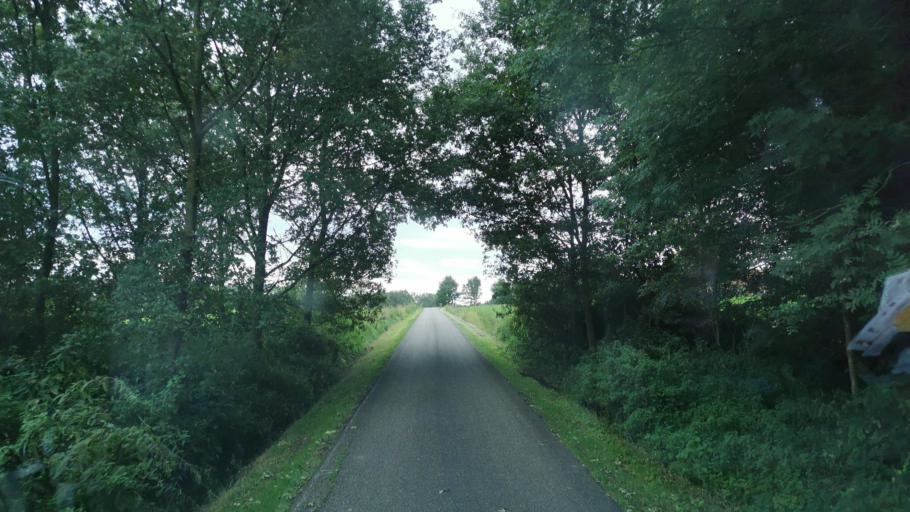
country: NL
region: Overijssel
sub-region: Gemeente Oldenzaal
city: Oldenzaal
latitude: 52.3341
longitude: 6.9848
